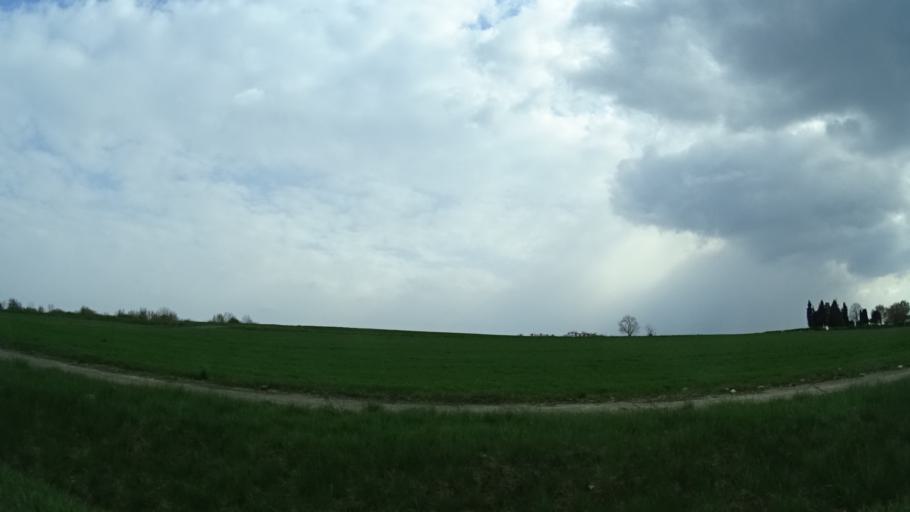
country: DE
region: Rheinland-Pfalz
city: Auen
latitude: 49.8525
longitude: 7.5974
